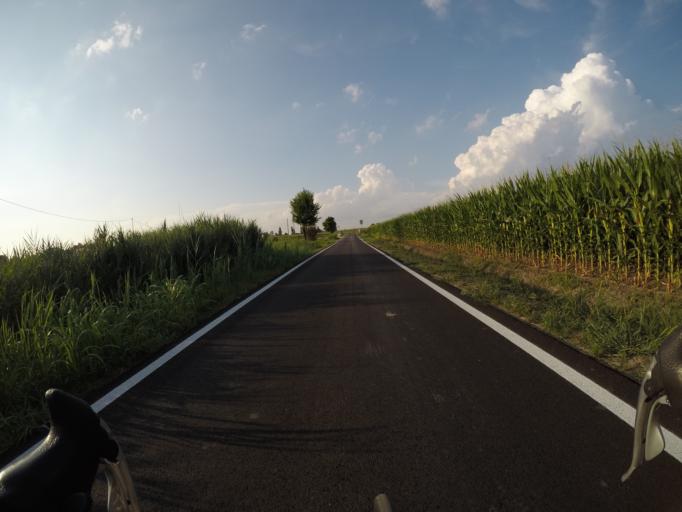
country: IT
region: Veneto
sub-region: Provincia di Rovigo
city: San Bellino
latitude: 45.0428
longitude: 11.5904
